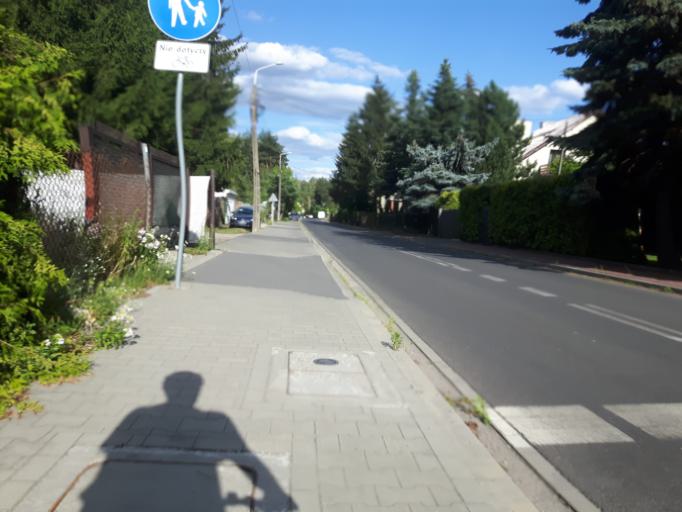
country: PL
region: Masovian Voivodeship
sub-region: Powiat wolominski
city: Zabki
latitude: 52.2945
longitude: 21.1271
